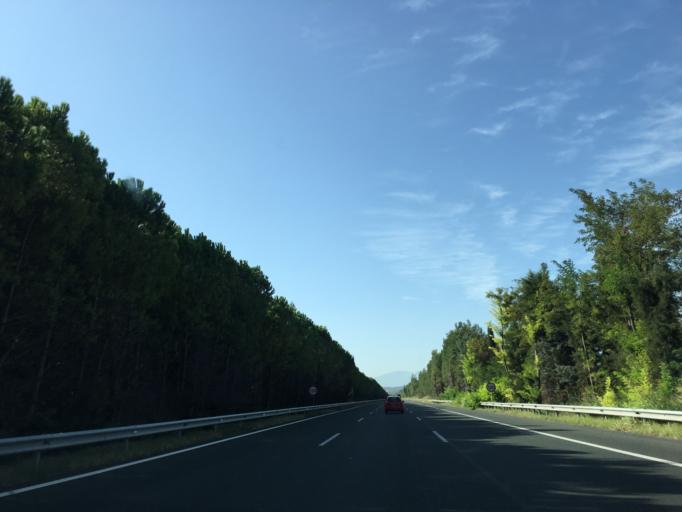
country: GR
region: Central Macedonia
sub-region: Nomos Pierias
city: Aiginio
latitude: 40.5093
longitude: 22.5688
